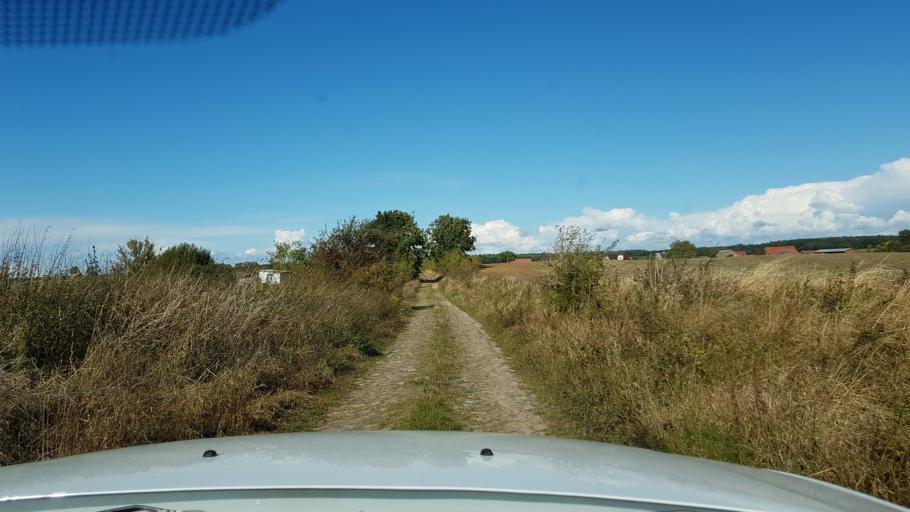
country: PL
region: West Pomeranian Voivodeship
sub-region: Powiat gryfinski
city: Banie
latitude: 53.1371
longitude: 14.6445
